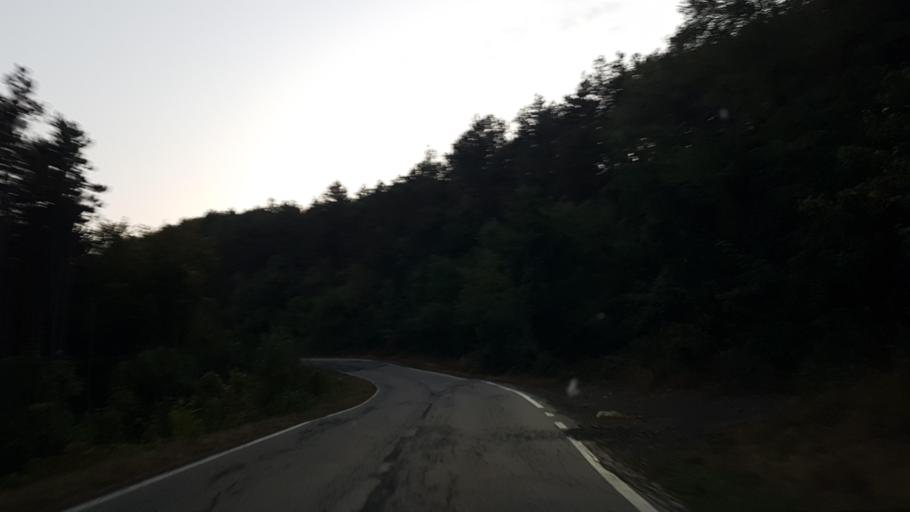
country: IT
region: Emilia-Romagna
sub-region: Provincia di Parma
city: Tornolo
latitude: 44.4346
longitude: 9.6283
